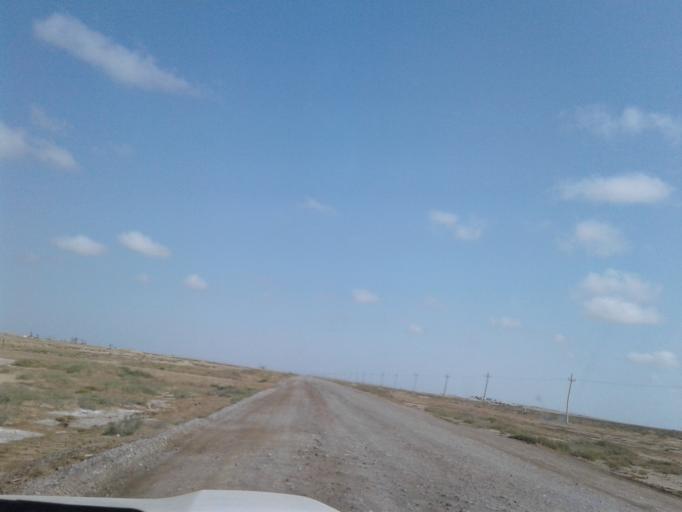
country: IR
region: Golestan
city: Gomishan
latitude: 37.7017
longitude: 53.9395
